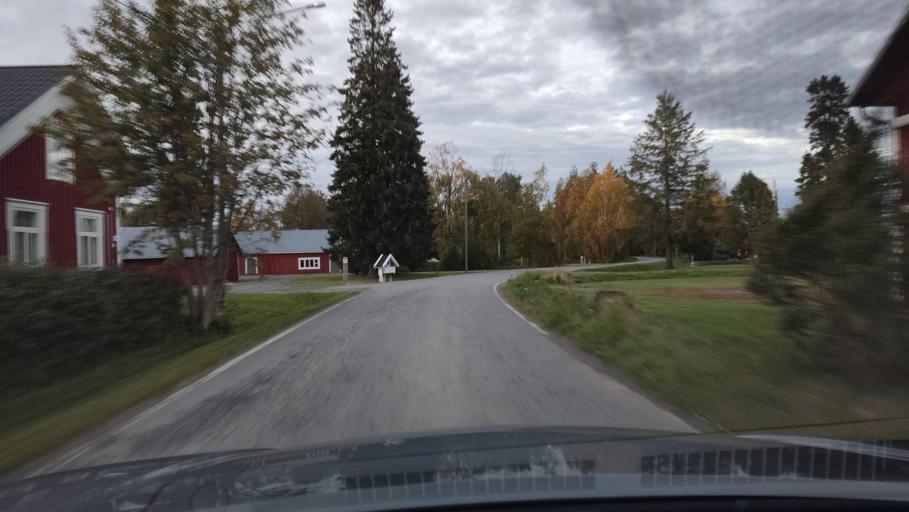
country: FI
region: Ostrobothnia
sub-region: Sydosterbotten
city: Kristinestad
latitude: 62.2614
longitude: 21.5080
